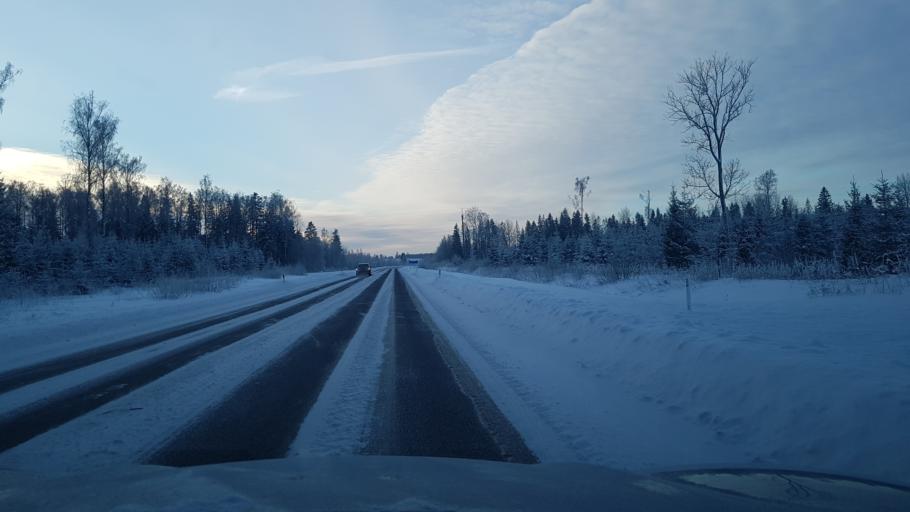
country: EE
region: Ida-Virumaa
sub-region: Johvi vald
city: Johvi
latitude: 59.3446
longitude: 27.4679
